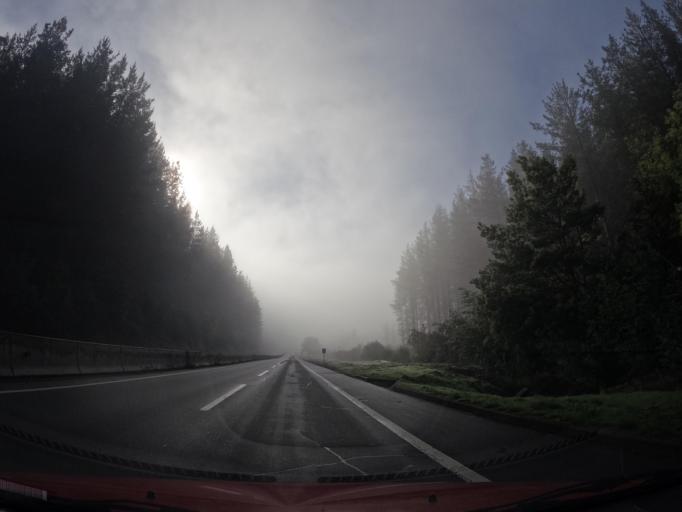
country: CL
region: Biobio
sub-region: Provincia de Concepcion
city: Penco
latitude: -36.7286
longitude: -72.8419
